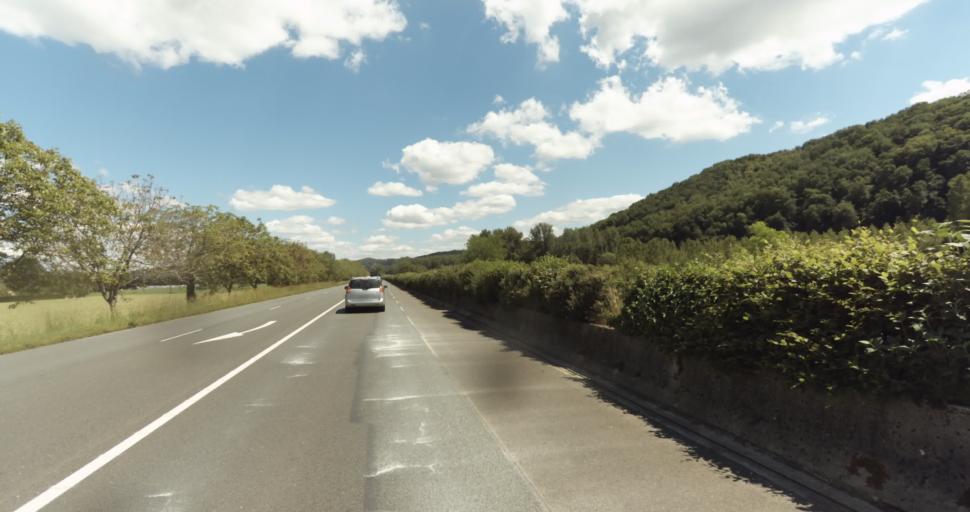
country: FR
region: Aquitaine
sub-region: Departement de la Dordogne
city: Belves
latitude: 44.8243
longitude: 0.9565
